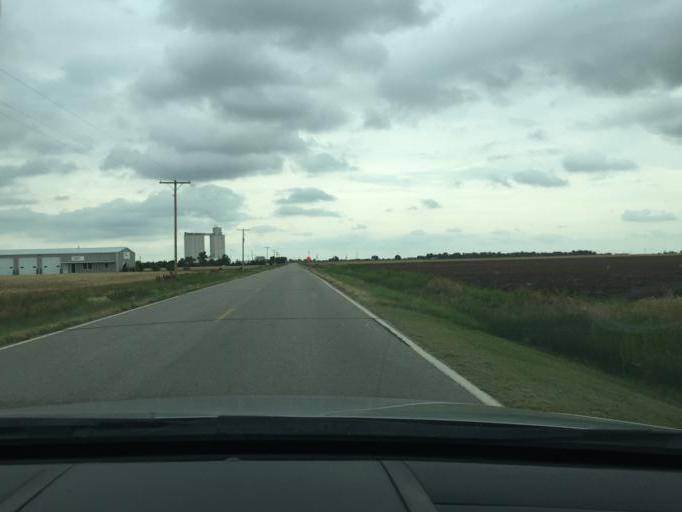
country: US
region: Kansas
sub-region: Reno County
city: South Hutchinson
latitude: 38.0004
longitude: -98.0138
